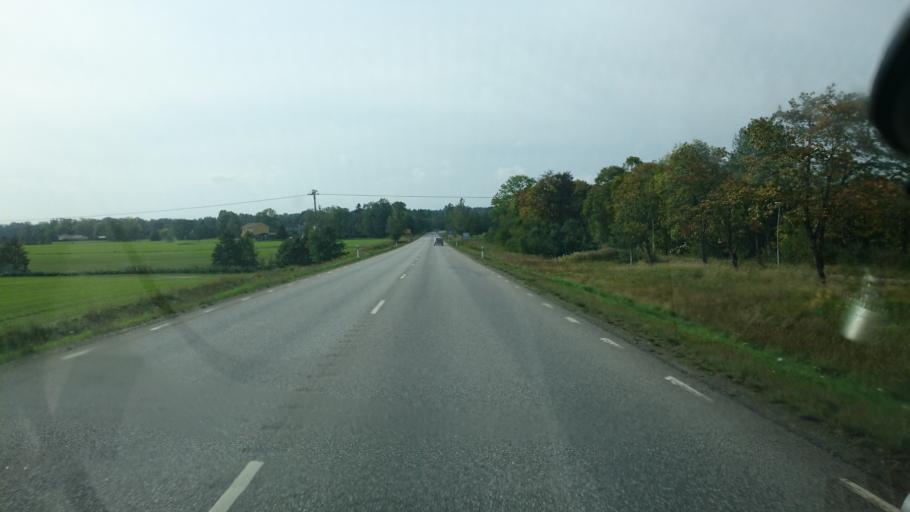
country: SE
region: Vaestra Goetaland
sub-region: Alingsas Kommun
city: Sollebrunn
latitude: 58.0903
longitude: 12.4974
